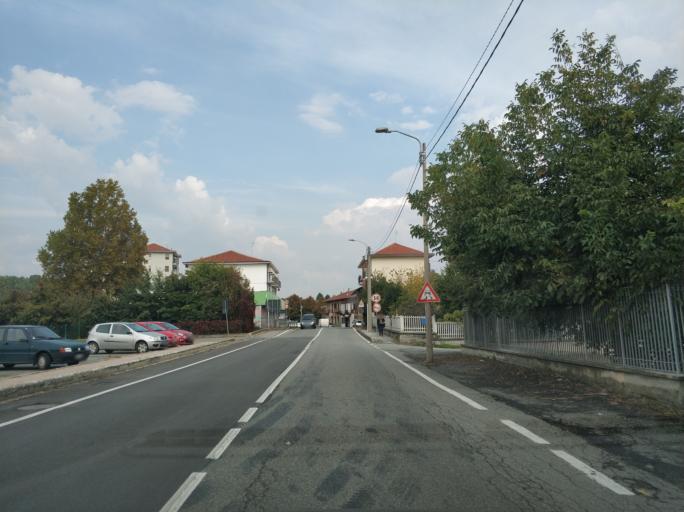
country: IT
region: Piedmont
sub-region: Provincia di Torino
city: San Carlo Canavese
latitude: 45.2390
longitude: 7.6051
